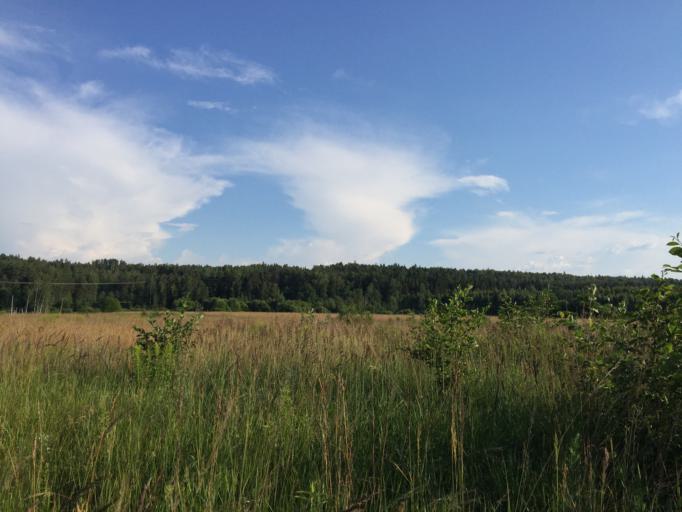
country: LV
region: Krimulda
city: Ragana
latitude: 57.1480
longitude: 24.7589
